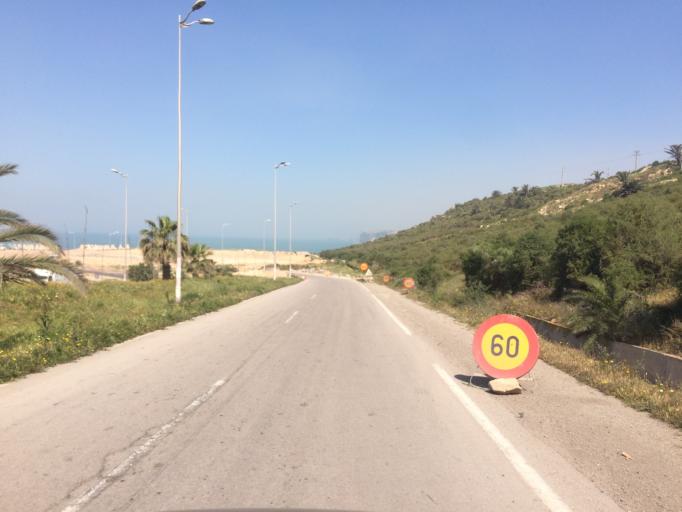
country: MA
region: Doukkala-Abda
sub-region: El-Jadida
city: Moulay Abdallah
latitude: 33.1369
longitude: -8.6109
